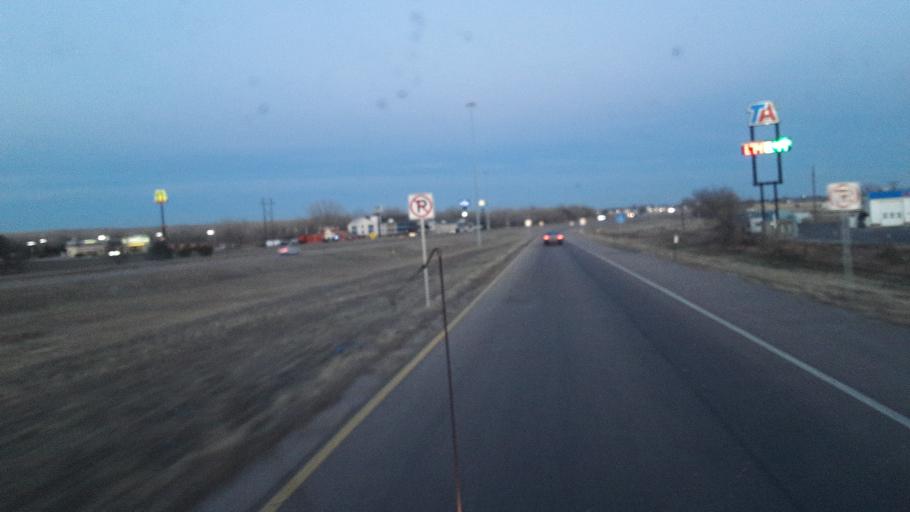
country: US
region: Nebraska
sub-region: Keith County
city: Ogallala
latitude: 41.1141
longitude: -101.7138
